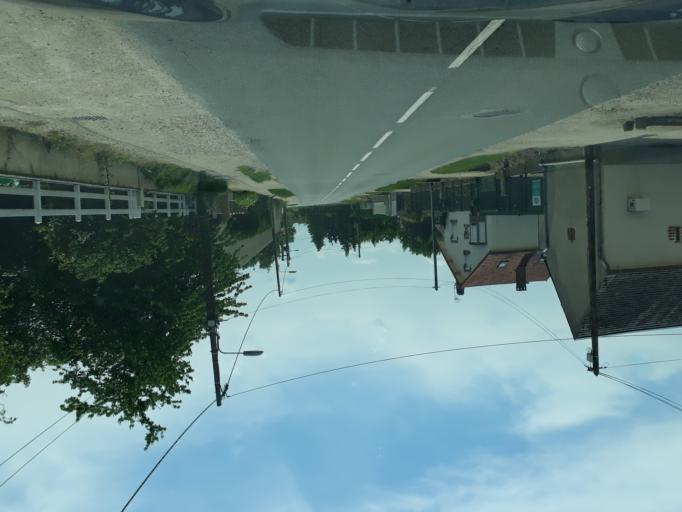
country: FR
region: Centre
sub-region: Departement du Loiret
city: Sandillon
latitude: 47.8414
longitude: 2.0349
